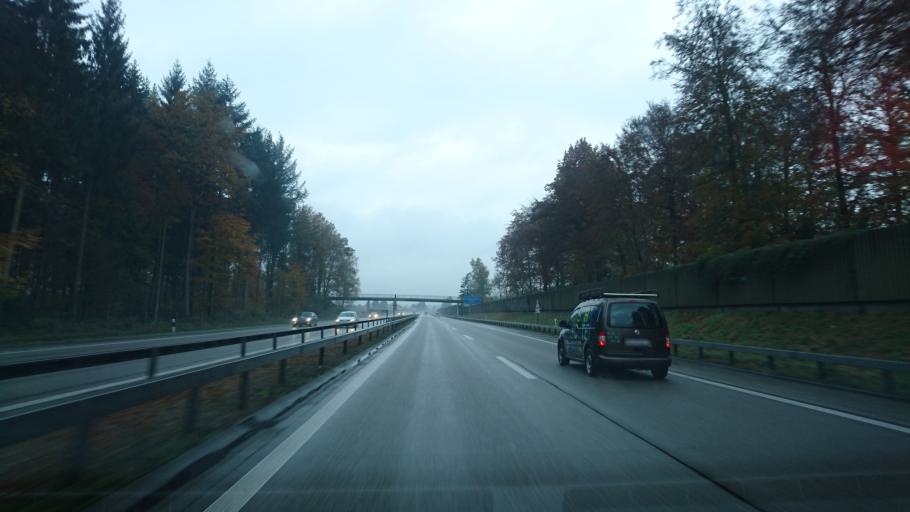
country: CH
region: Solothurn
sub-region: Bezirk Wasseramt
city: Kriegstetten
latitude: 47.1564
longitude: 7.5912
